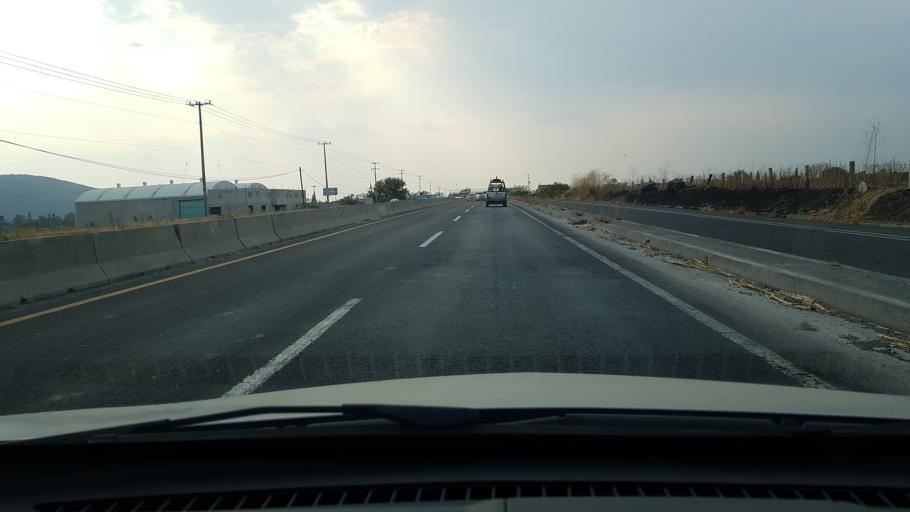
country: MX
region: Morelos
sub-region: Ayala
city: Unidad Habitacional Mariano Matamoros
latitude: 18.7418
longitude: -98.8334
